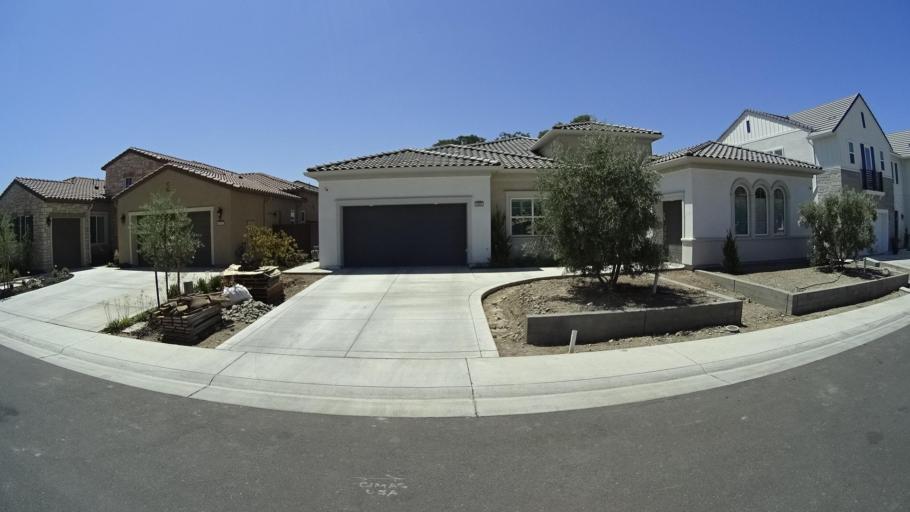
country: US
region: California
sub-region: Placer County
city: Rocklin
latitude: 38.8358
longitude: -121.2520
